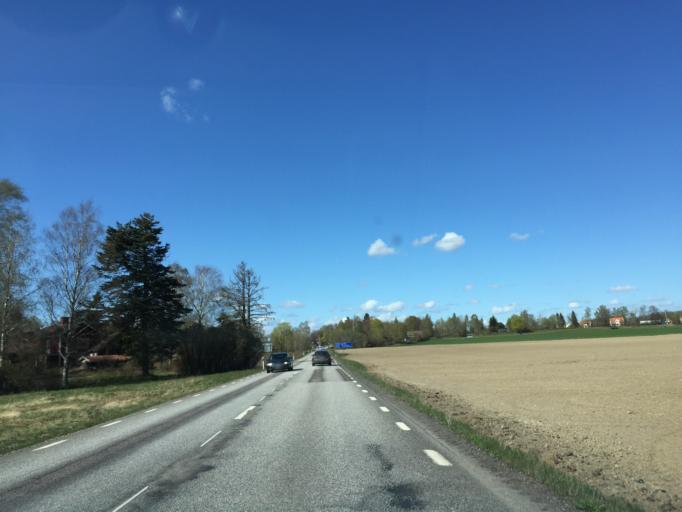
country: SE
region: OErebro
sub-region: Hallsbergs Kommun
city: Skollersta
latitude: 59.1253
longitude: 15.3276
